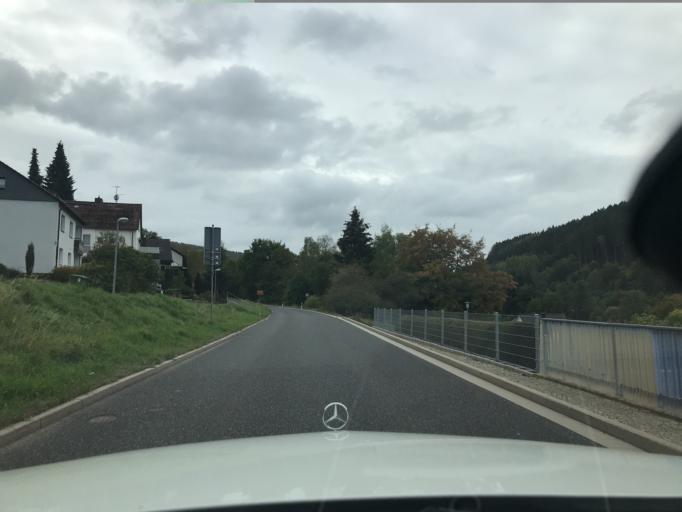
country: DE
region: Hesse
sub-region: Regierungsbezirk Kassel
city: Helsa
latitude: 51.2553
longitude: 9.6875
